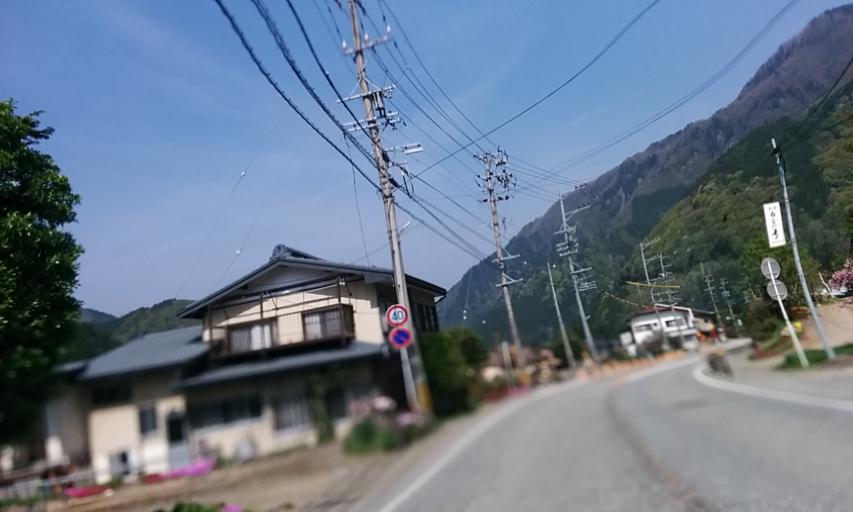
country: JP
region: Gifu
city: Takayama
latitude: 36.2432
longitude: 137.5189
